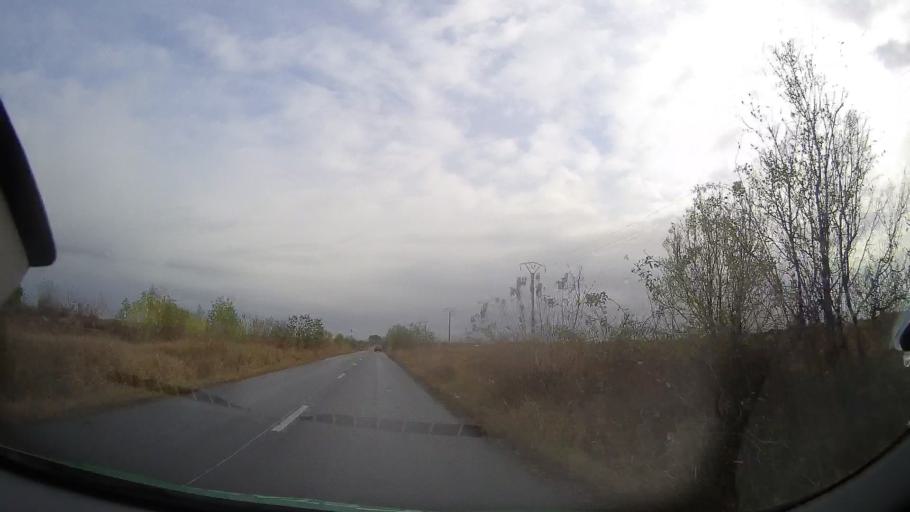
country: RO
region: Ialomita
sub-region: Comuna Maia
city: Maia
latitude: 44.7494
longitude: 26.3924
